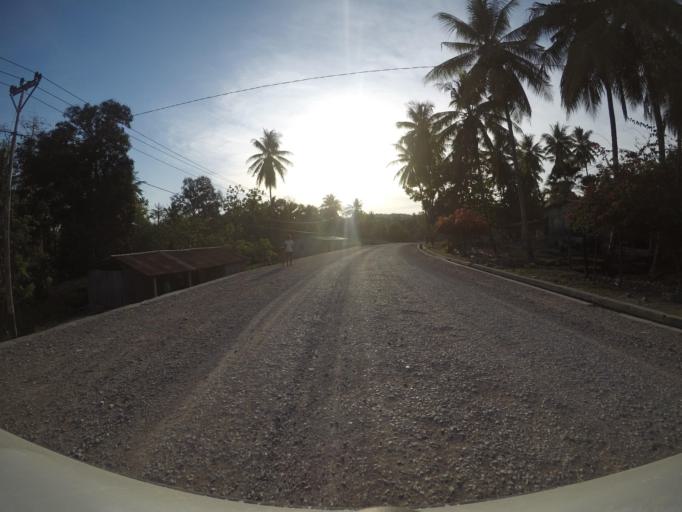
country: TL
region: Viqueque
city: Viqueque
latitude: -8.8425
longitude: 126.5151
